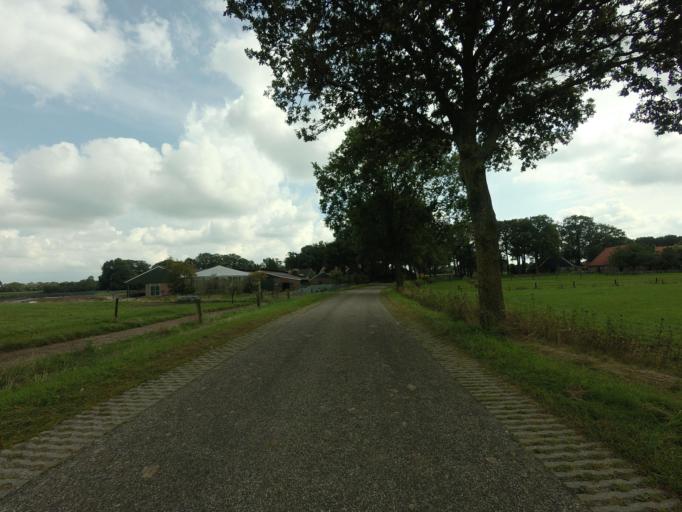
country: DE
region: Lower Saxony
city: Nordhorn
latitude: 52.3595
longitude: 7.0180
